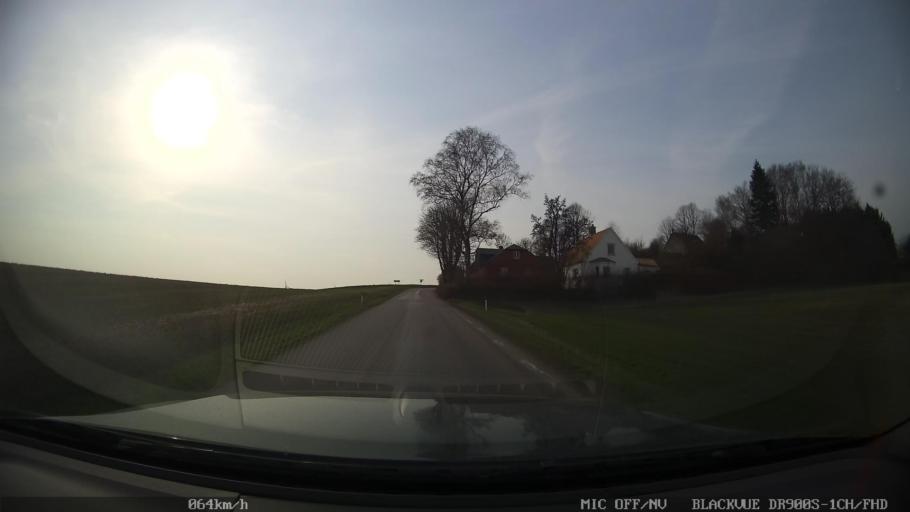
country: SE
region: Skane
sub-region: Ystads Kommun
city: Ystad
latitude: 55.4655
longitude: 13.8181
